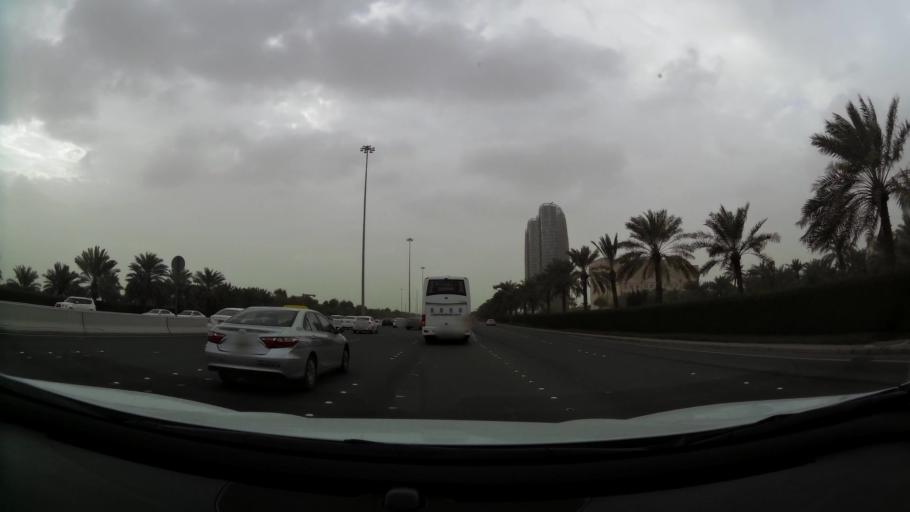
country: AE
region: Abu Dhabi
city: Abu Dhabi
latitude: 24.4613
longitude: 54.3992
